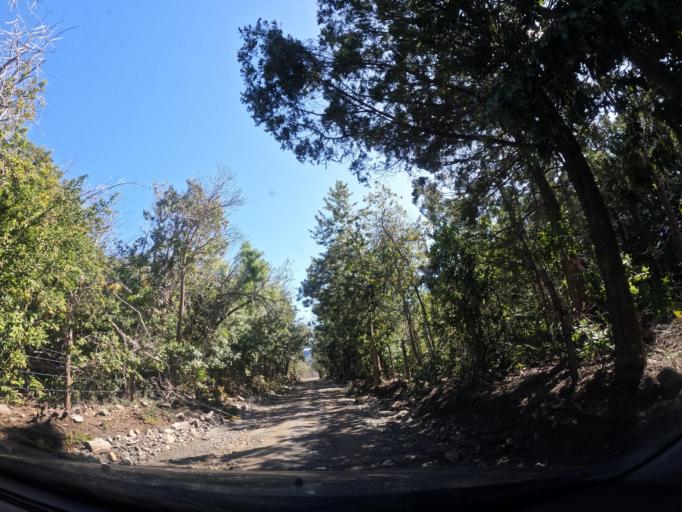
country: CL
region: Maule
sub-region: Provincia de Linares
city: Longavi
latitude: -36.2419
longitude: -71.3503
